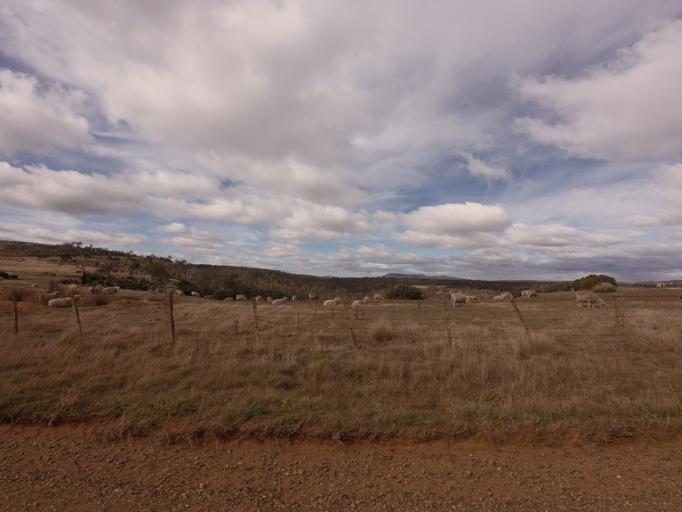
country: AU
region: Tasmania
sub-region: Brighton
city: Bridgewater
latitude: -42.4252
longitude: 147.3899
